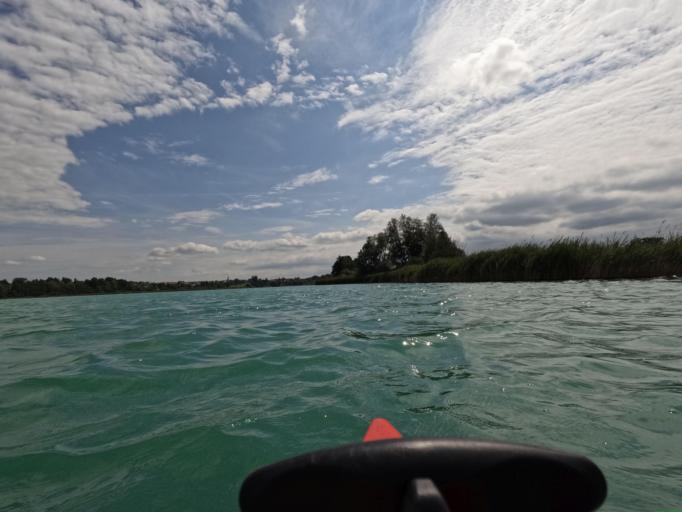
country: DE
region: Bavaria
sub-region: Upper Bavaria
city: Taching am See
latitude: 47.9586
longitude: 12.7372
